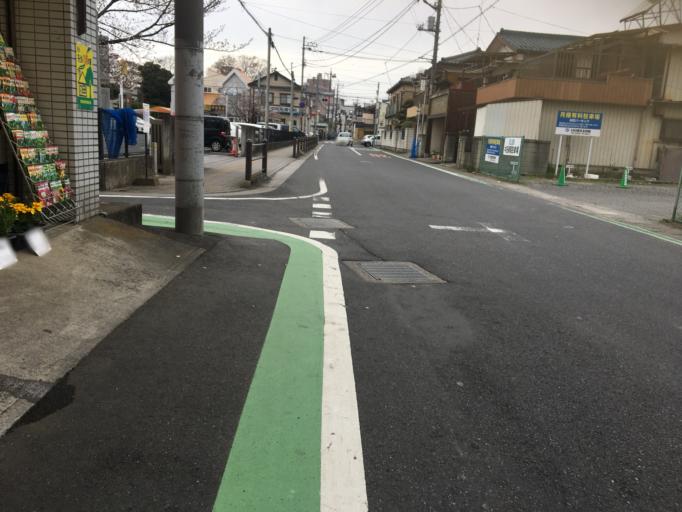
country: JP
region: Saitama
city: Kazo
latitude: 36.1240
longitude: 139.6002
